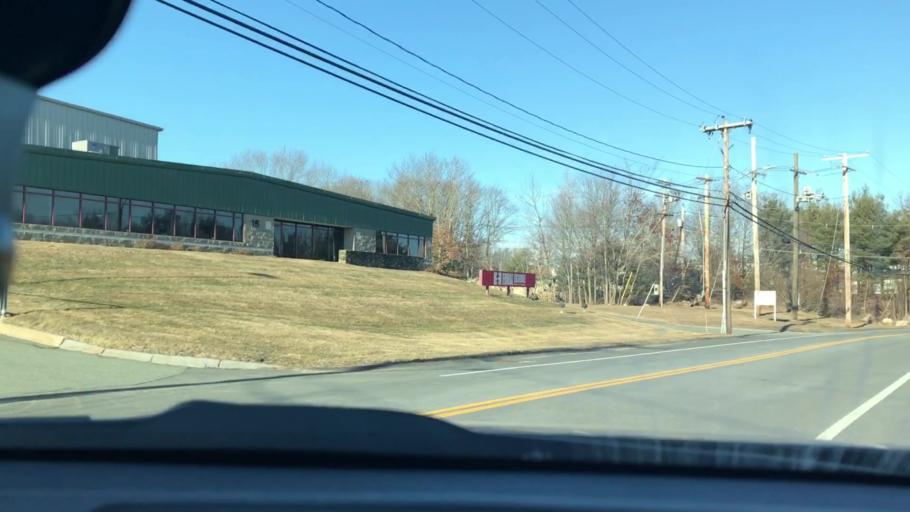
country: US
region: Massachusetts
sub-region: Norfolk County
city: Randolph
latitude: 42.1650
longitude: -71.0746
